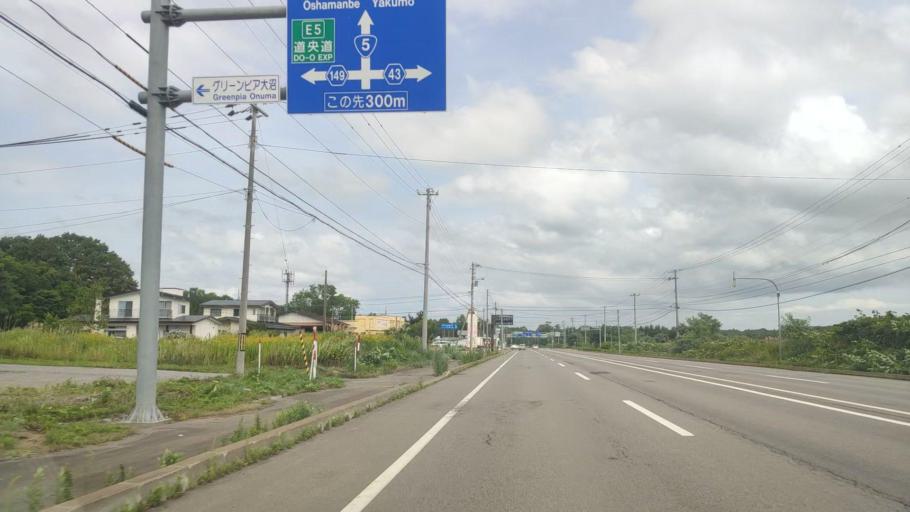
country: JP
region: Hokkaido
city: Nanae
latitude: 42.0045
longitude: 140.6328
